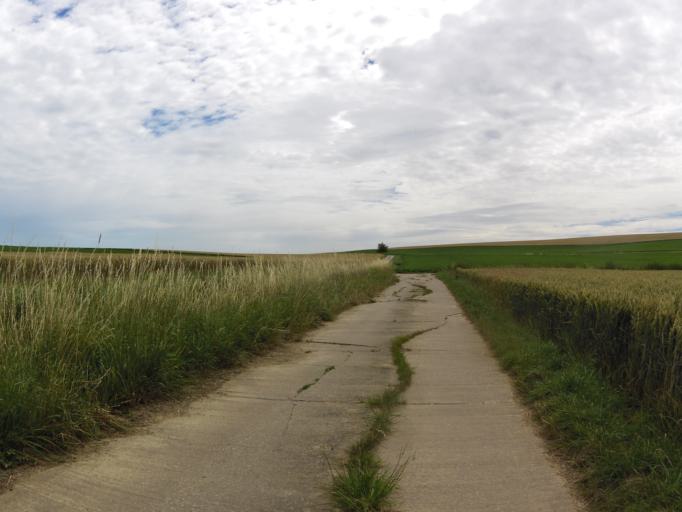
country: DE
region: Bavaria
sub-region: Regierungsbezirk Unterfranken
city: Reichenberg
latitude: 49.7123
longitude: 9.8957
